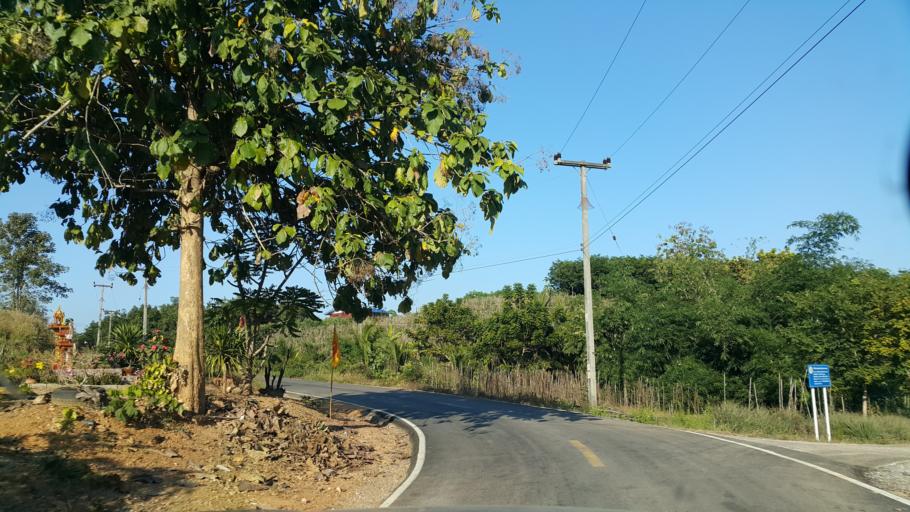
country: TH
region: Sukhothai
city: Thung Saliam
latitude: 17.4015
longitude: 99.5129
